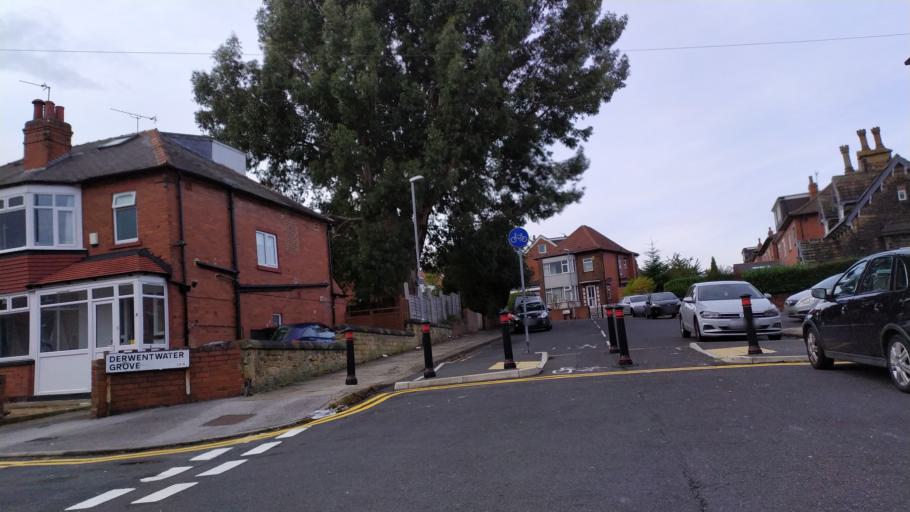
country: GB
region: England
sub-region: City and Borough of Leeds
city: Leeds
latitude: 53.8197
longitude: -1.5819
